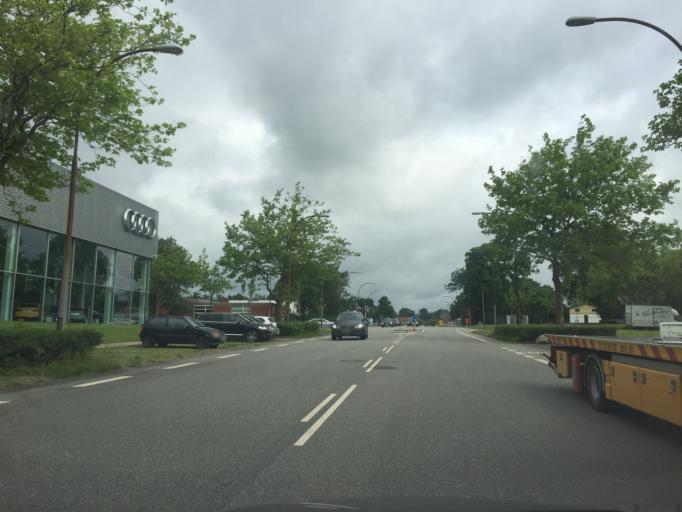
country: DK
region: Capital Region
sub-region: Herlev Kommune
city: Herlev
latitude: 55.7327
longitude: 12.4615
